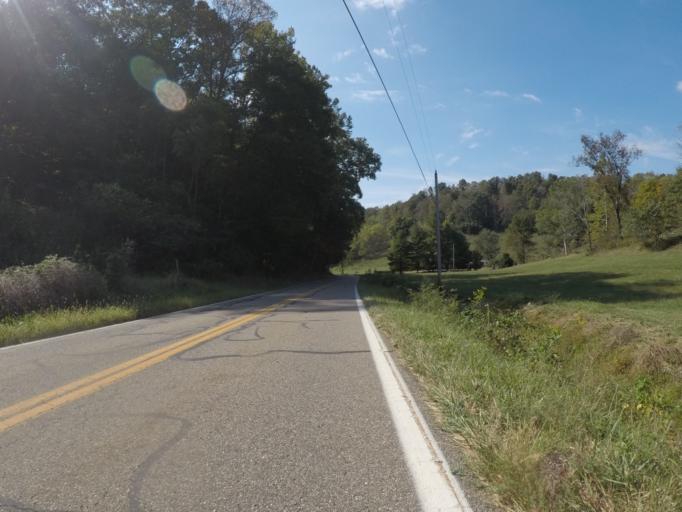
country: US
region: West Virginia
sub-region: Cabell County
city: Lesage
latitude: 38.6407
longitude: -82.4321
